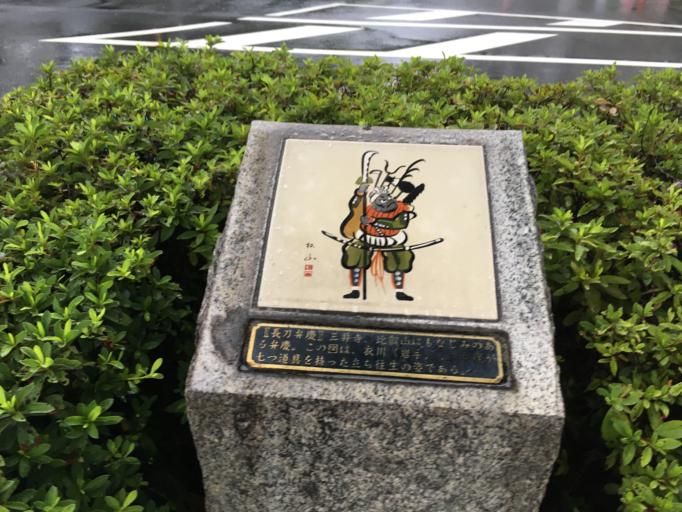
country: JP
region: Shiga Prefecture
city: Otsu-shi
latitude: 35.0174
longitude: 135.8554
